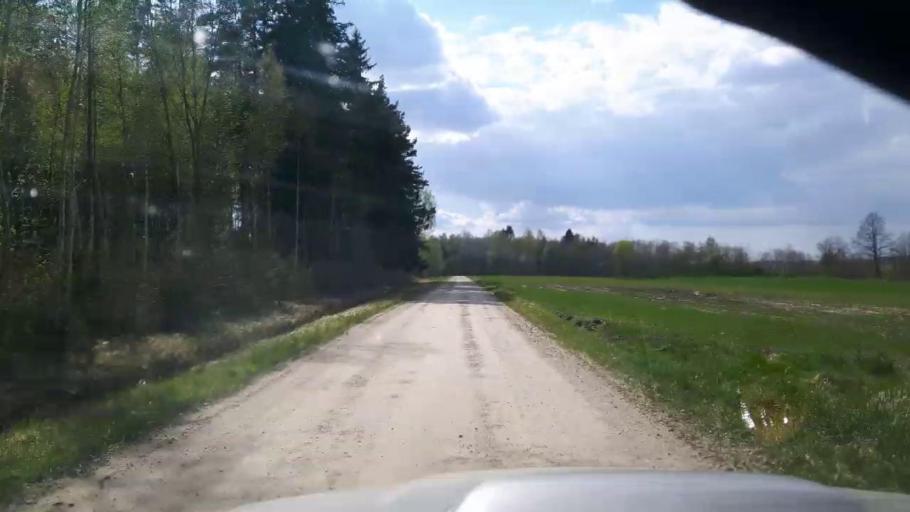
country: EE
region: Paernumaa
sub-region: Sindi linn
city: Sindi
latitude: 58.4307
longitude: 24.7730
